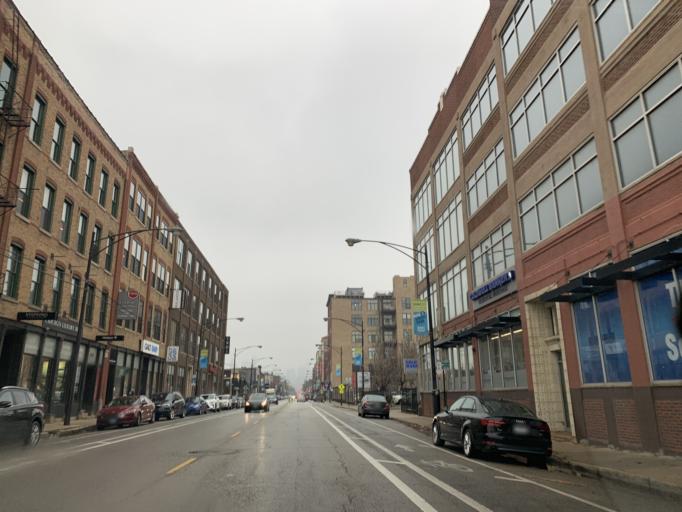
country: US
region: Illinois
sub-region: Cook County
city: Chicago
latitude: 41.9160
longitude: -87.6566
